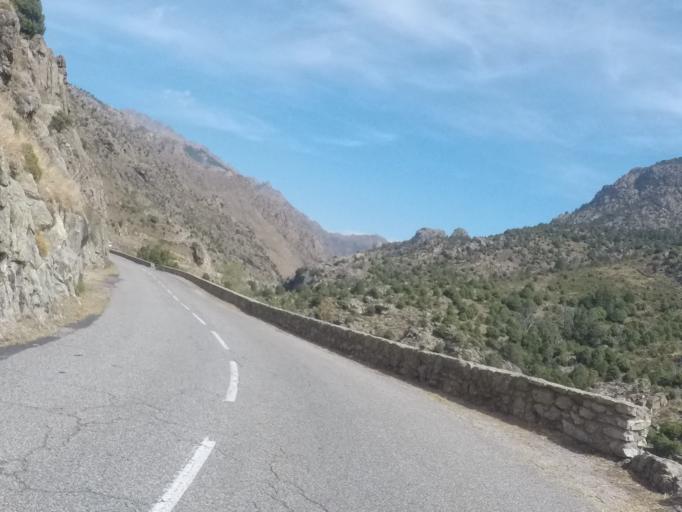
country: FR
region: Corsica
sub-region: Departement de la Haute-Corse
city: Corte
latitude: 42.3476
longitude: 9.0491
